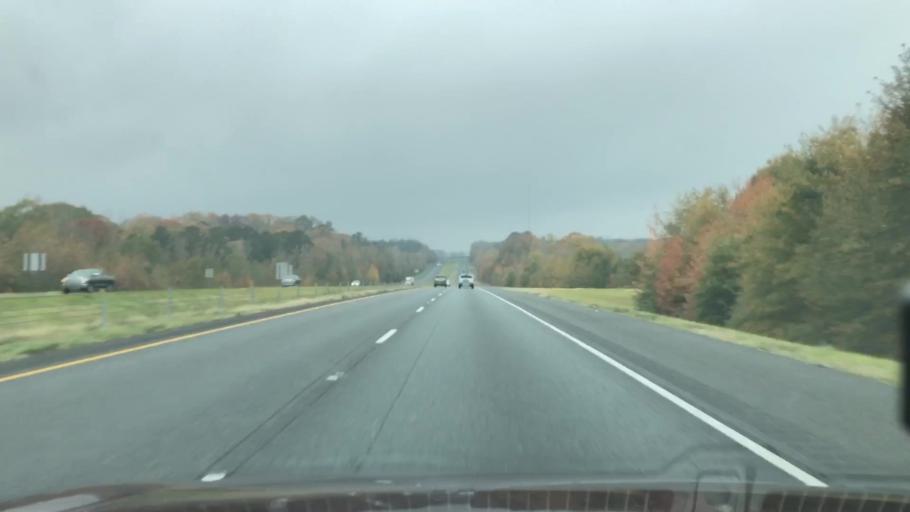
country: US
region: Louisiana
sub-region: Lincoln Parish
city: Grambling
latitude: 32.5485
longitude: -92.7892
